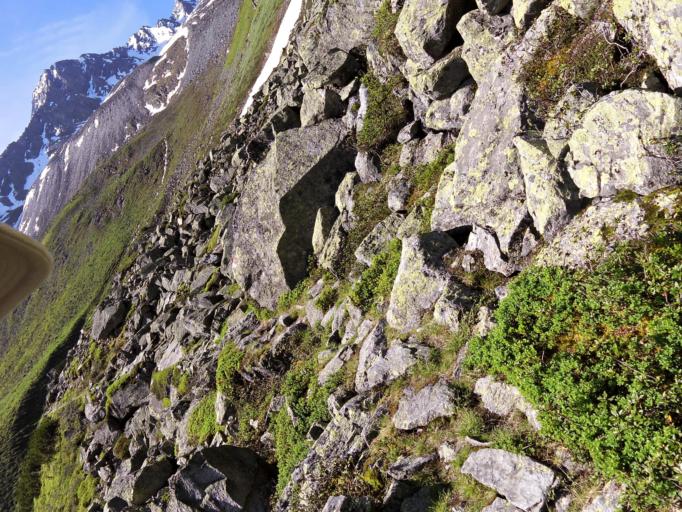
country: AT
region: Tyrol
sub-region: Politischer Bezirk Innsbruck Land
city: Gries im Sellrain
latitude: 47.0842
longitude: 11.1825
